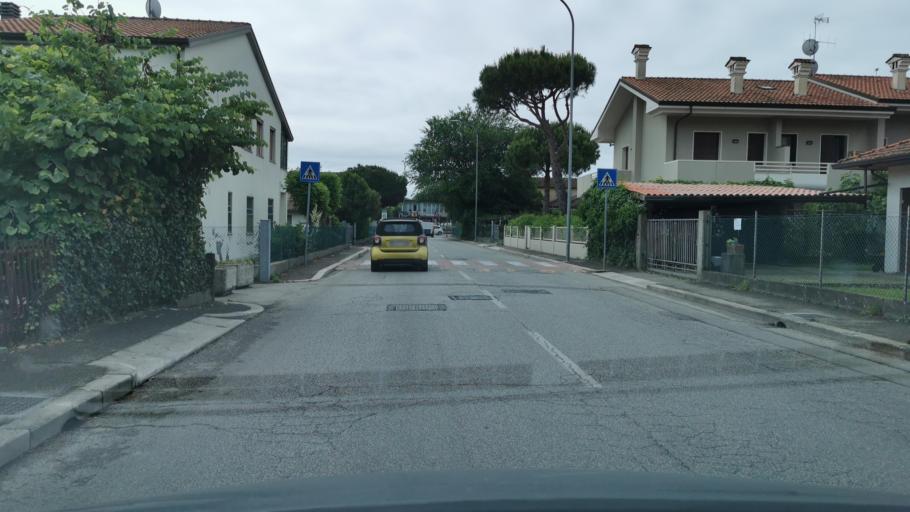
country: IT
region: Emilia-Romagna
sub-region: Provincia di Ravenna
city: Cervia
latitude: 44.2629
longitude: 12.3465
